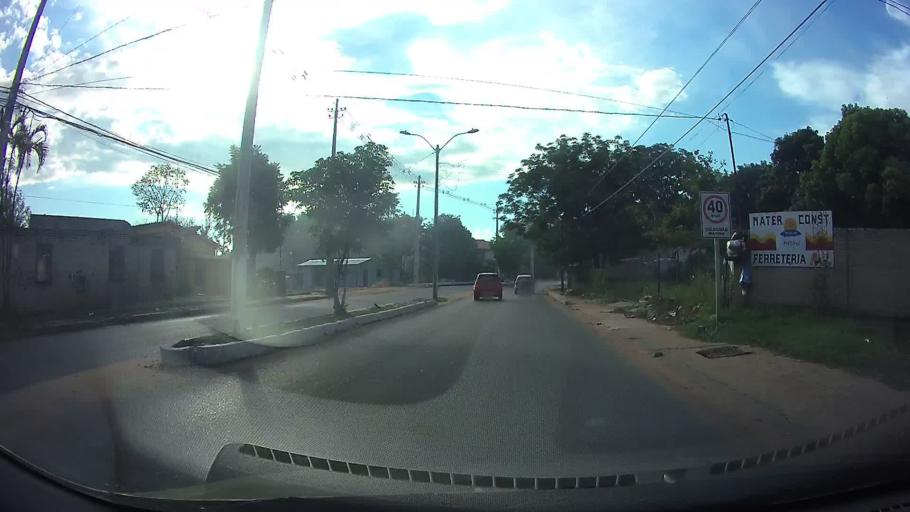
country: PY
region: Central
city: San Antonio
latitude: -25.4190
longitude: -57.5700
